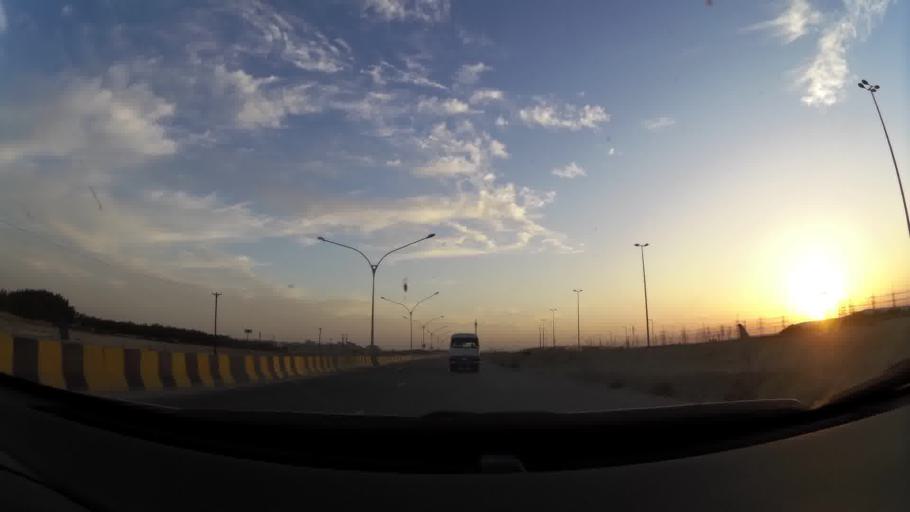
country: KW
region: Al Asimah
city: Ar Rabiyah
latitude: 29.3413
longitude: 47.8012
